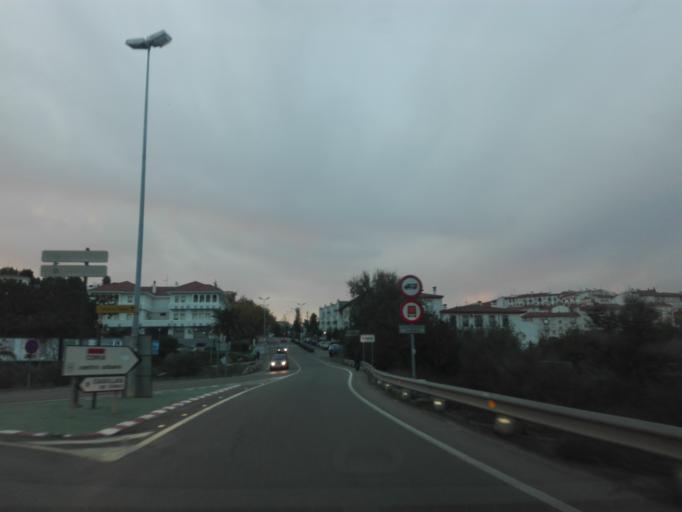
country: ES
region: Extremadura
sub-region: Provincia de Caceres
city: Coria
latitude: 39.9809
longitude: -6.5288
